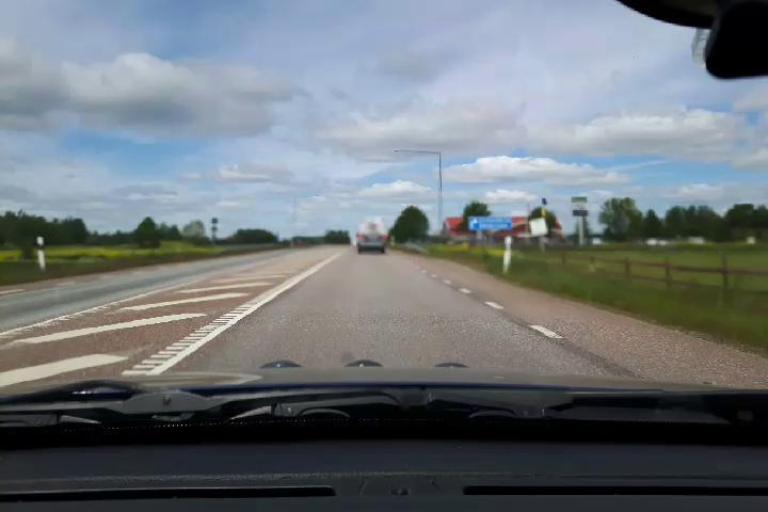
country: SE
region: Uppsala
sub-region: Uppsala Kommun
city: Gamla Uppsala
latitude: 59.9371
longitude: 17.5947
